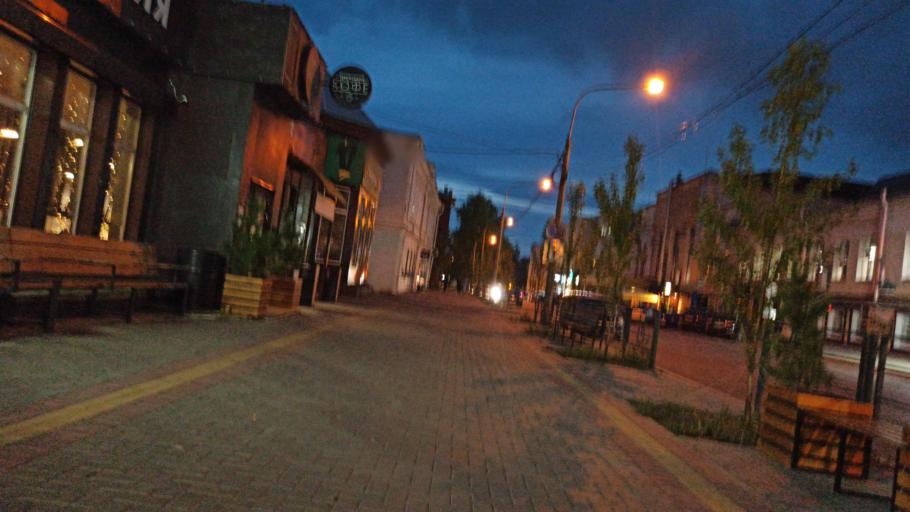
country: RU
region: Tomsk
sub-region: Tomskiy Rayon
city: Tomsk
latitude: 56.4640
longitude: 84.9574
